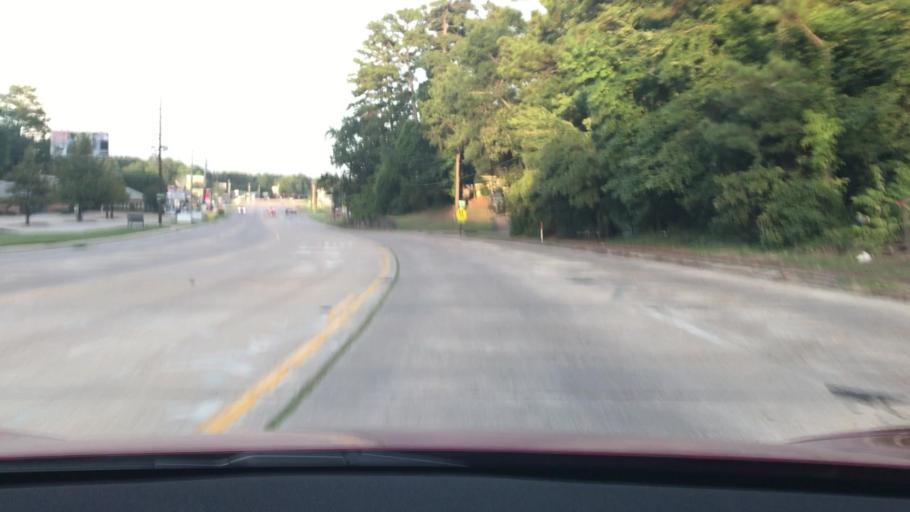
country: US
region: Louisiana
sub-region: Bossier Parish
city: Bossier City
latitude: 32.4015
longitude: -93.7834
